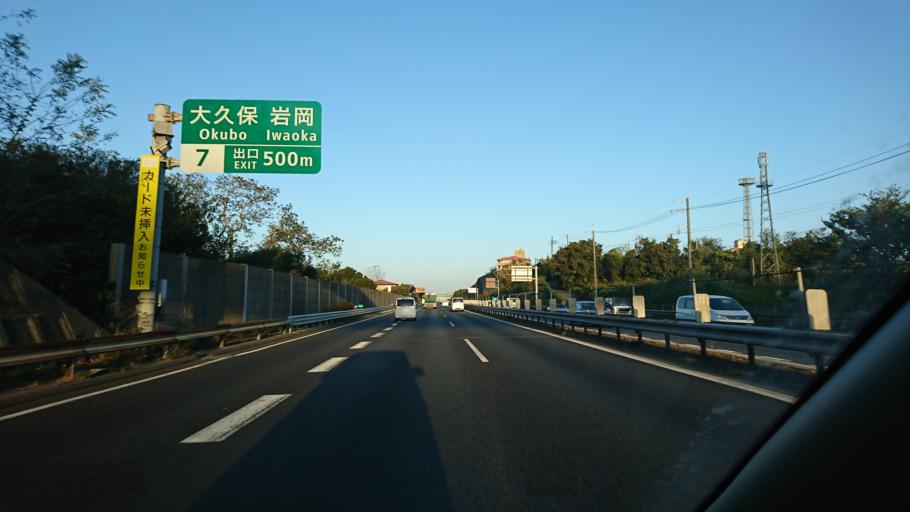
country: JP
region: Hyogo
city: Akashi
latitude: 34.7069
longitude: 134.9504
